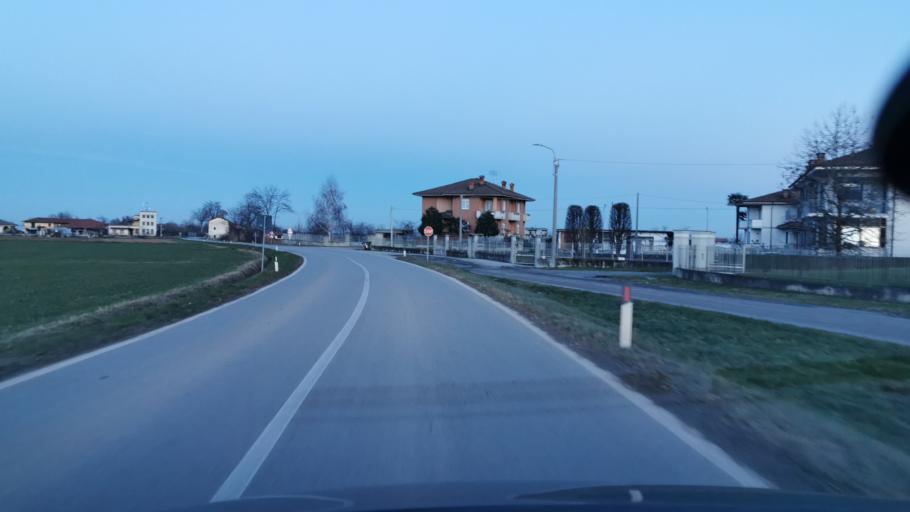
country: IT
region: Piedmont
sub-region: Provincia di Cuneo
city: Caraglio
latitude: 44.4316
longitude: 7.4508
